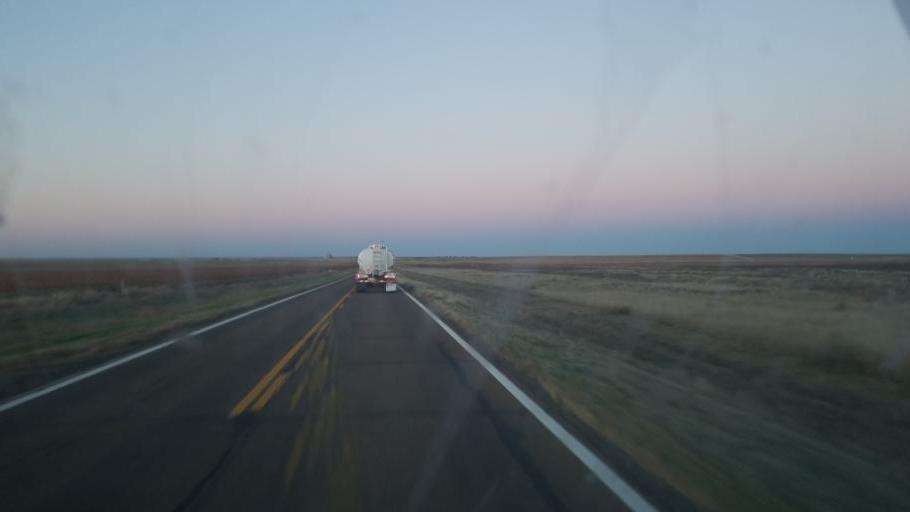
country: US
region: Kansas
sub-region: Wallace County
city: Sharon Springs
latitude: 38.9303
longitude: -101.5462
